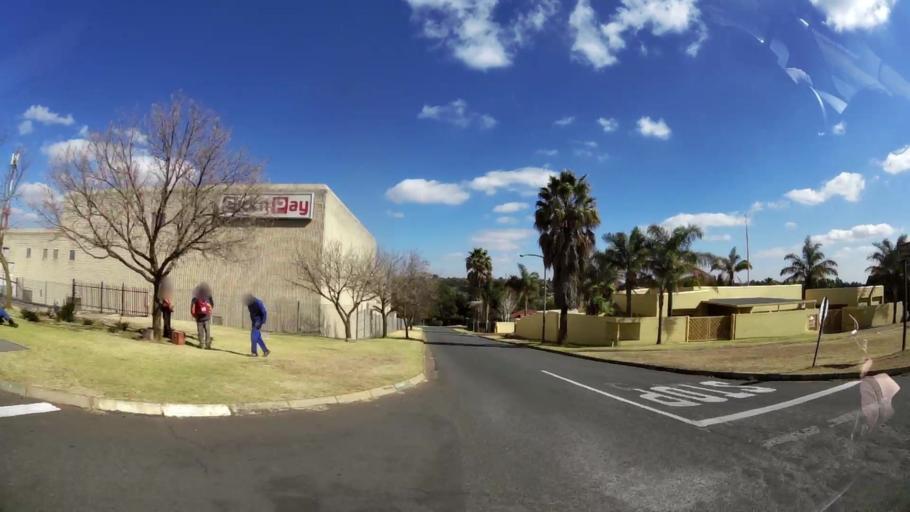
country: ZA
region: Gauteng
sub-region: West Rand District Municipality
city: Krugersdorp
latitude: -26.0961
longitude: 27.8036
